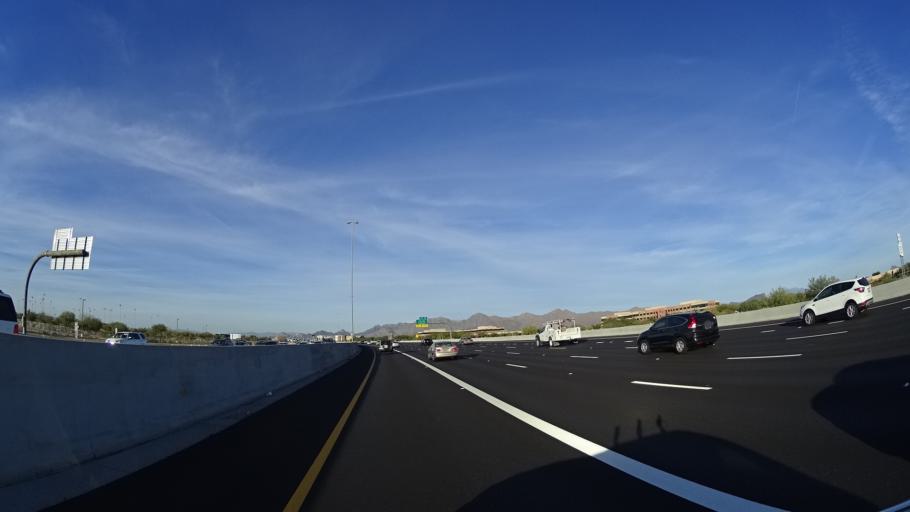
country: US
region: Arizona
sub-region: Maricopa County
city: Scottsdale
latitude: 33.5436
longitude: -111.8802
